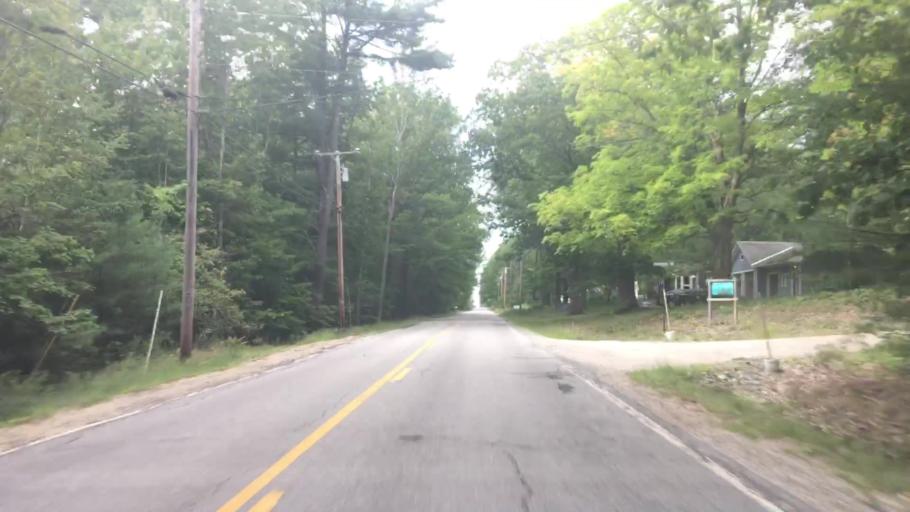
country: US
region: Maine
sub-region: Oxford County
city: Oxford
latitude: 44.0414
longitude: -70.5411
